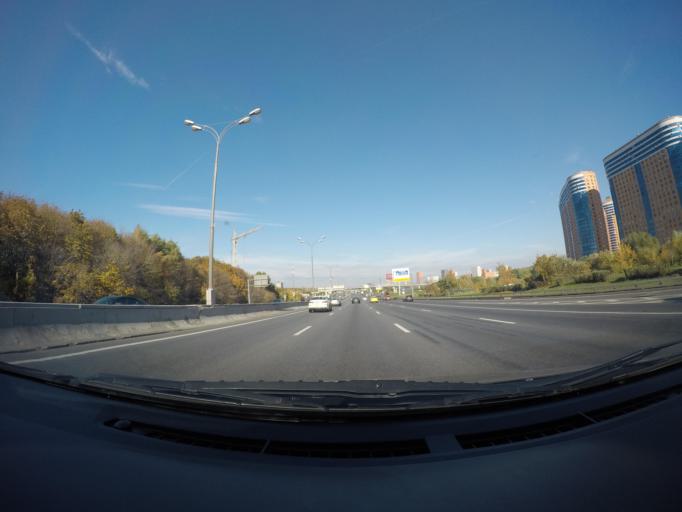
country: RU
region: Moscow
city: Ivanovskoye
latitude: 55.7722
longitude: 37.8434
